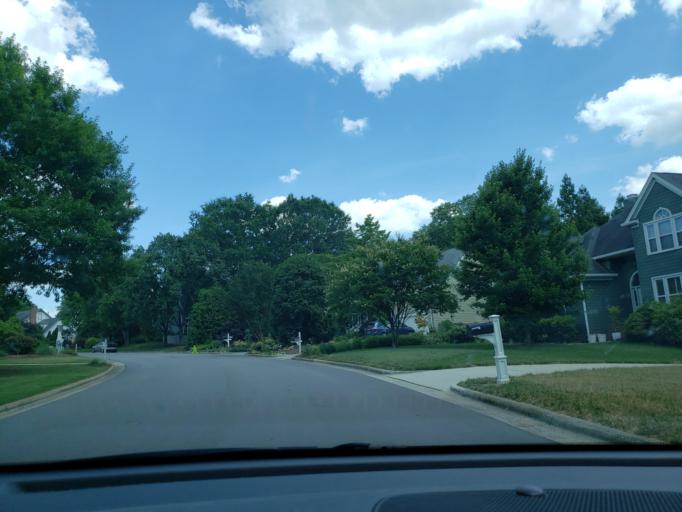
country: US
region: North Carolina
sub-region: Orange County
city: Chapel Hill
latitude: 35.9688
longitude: -78.9887
